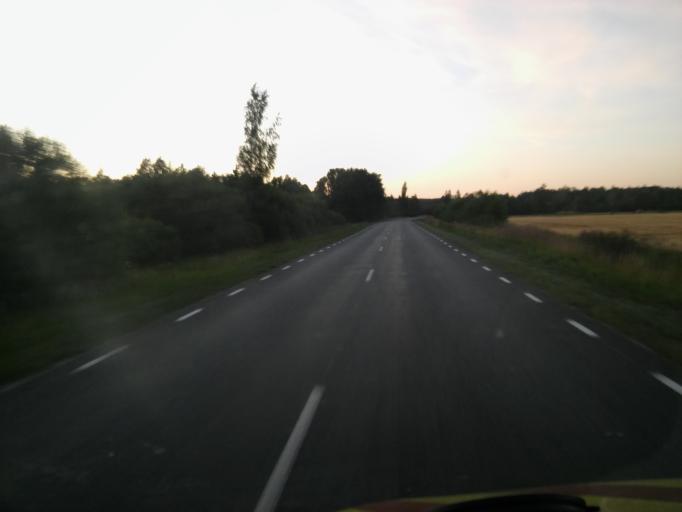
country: EE
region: Paernumaa
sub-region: Paikuse vald
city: Paikuse
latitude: 58.3187
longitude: 24.6843
